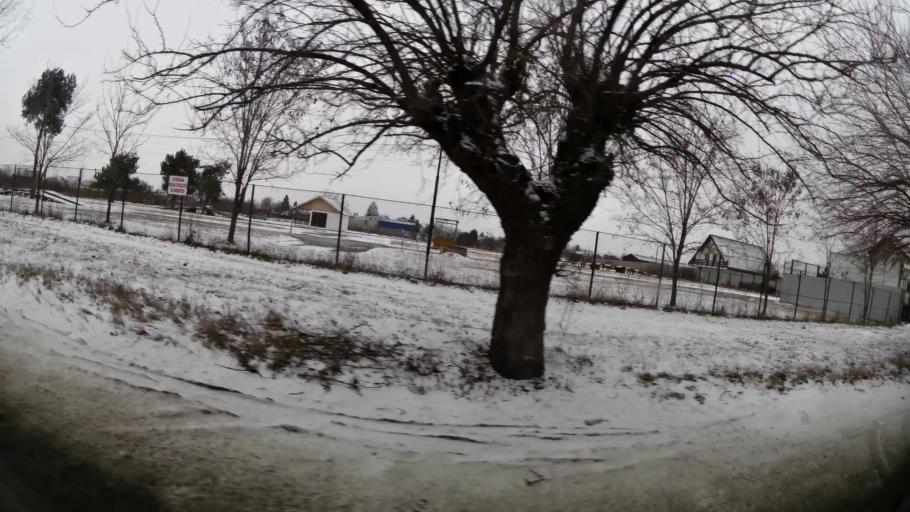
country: RO
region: Dambovita
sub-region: Comuna Ulmi
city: Ulmi
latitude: 44.9017
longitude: 25.4998
